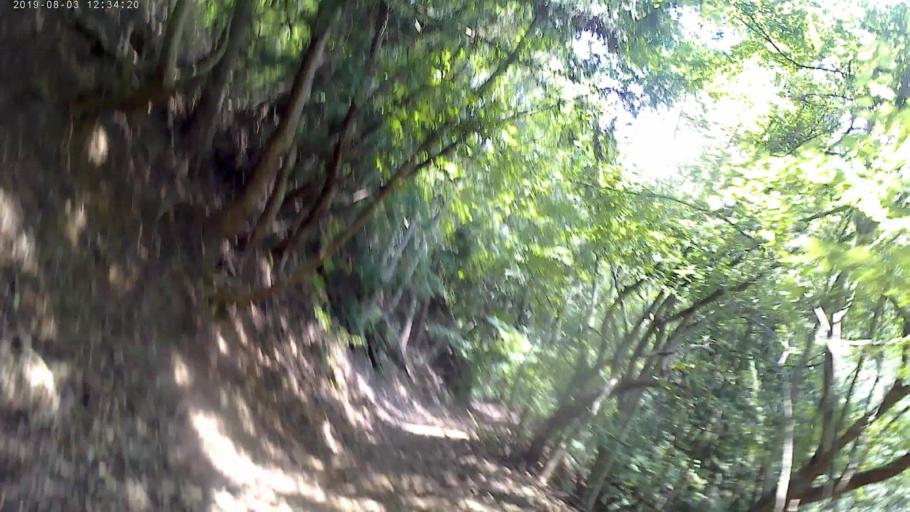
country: JP
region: Yamanashi
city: Enzan
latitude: 35.6078
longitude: 138.7917
